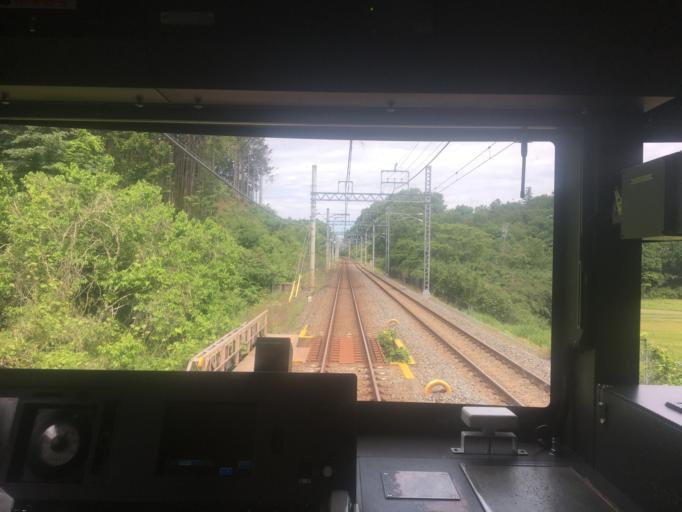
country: JP
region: Saitama
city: Ogawa
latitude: 36.0541
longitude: 139.3025
